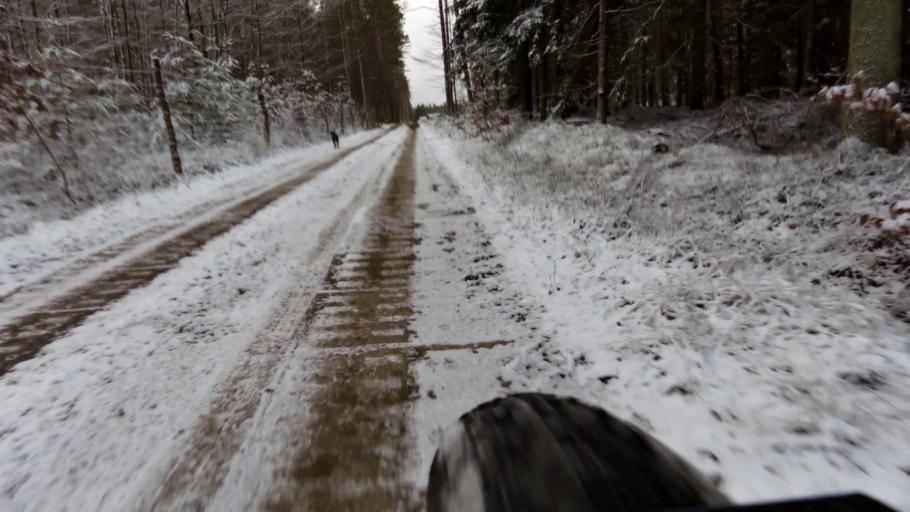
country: PL
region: West Pomeranian Voivodeship
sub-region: Powiat walecki
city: Miroslawiec
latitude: 53.3765
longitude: 16.1466
